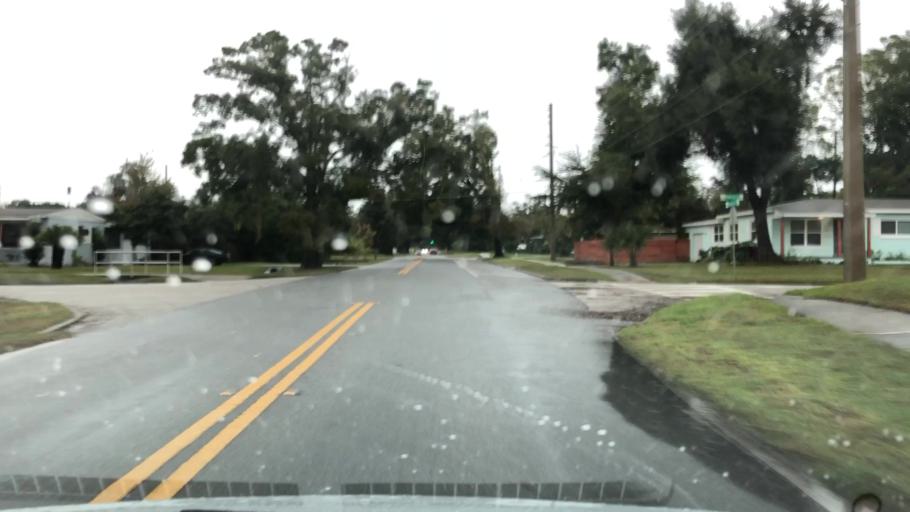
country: US
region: Florida
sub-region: Orange County
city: Conway
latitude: 28.5272
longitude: -81.3476
